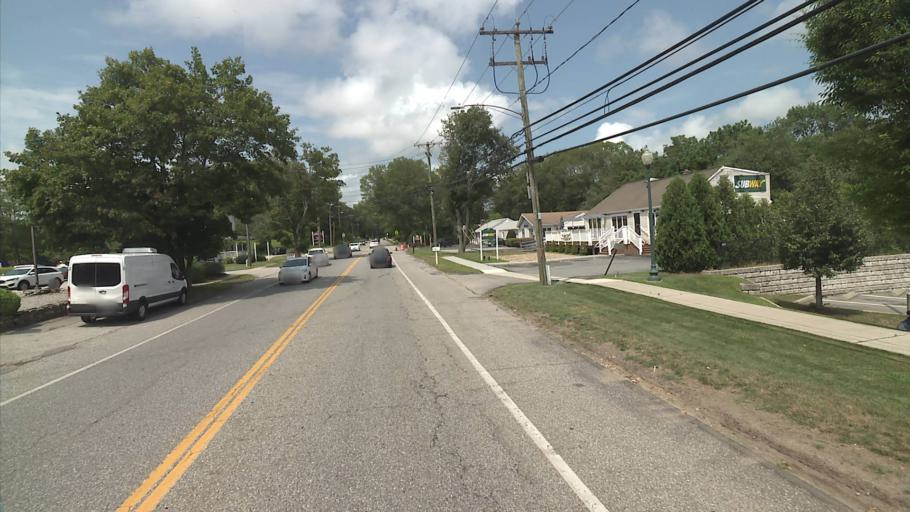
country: US
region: Connecticut
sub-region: New London County
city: Niantic
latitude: 41.3676
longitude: -72.2101
